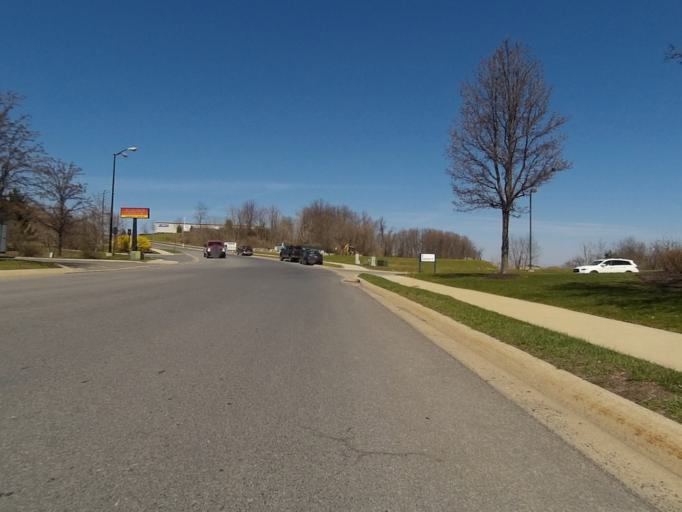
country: US
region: Pennsylvania
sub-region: Centre County
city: Park Forest Village
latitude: 40.8107
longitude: -77.9141
